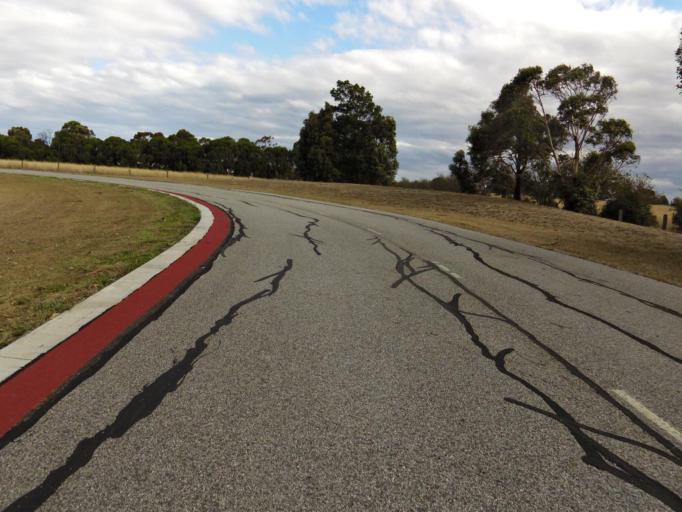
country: AU
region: Victoria
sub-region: Casey
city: Junction Village
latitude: -38.1273
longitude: 145.3110
